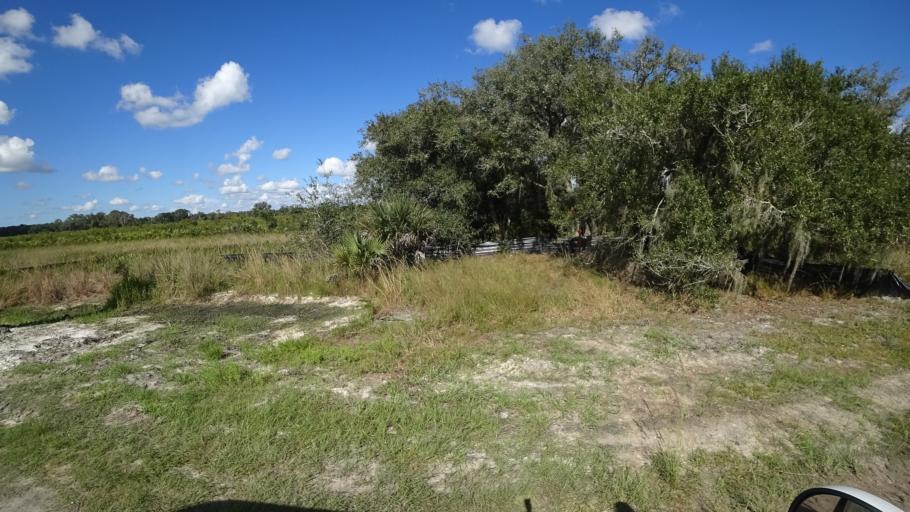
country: US
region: Florida
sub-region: Sarasota County
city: Lake Sarasota
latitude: 27.2472
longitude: -82.2818
